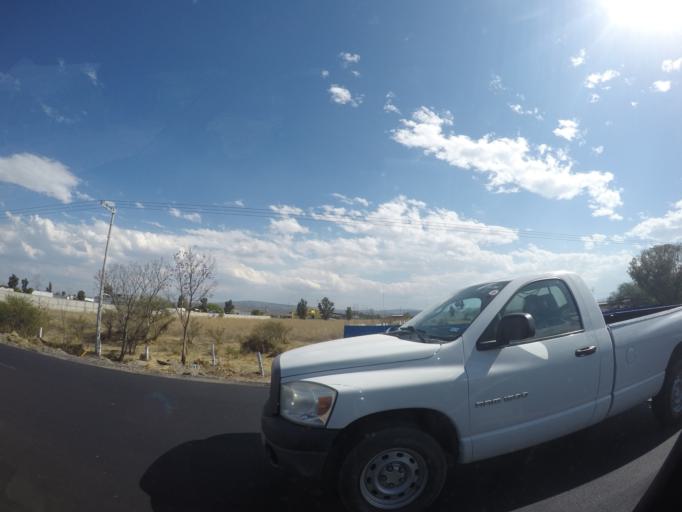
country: MX
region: Guanajuato
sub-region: Apaseo el Grande
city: La Labor
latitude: 20.5347
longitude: -100.7187
